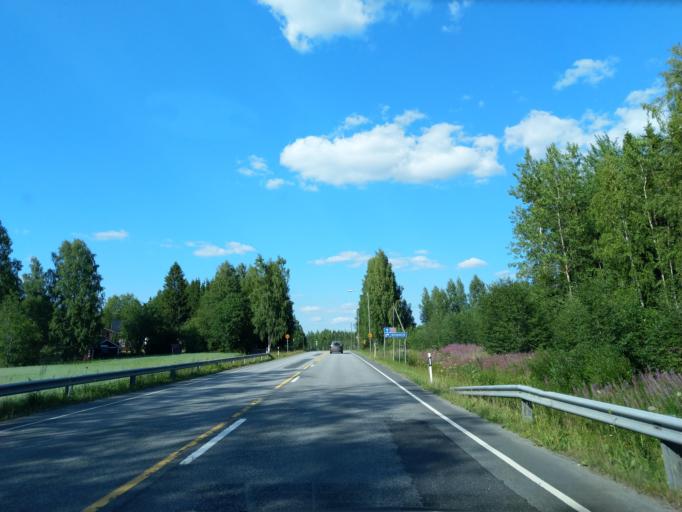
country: FI
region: Pirkanmaa
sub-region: Luoteis-Pirkanmaa
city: Kihnioe
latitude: 62.1733
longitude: 23.1666
